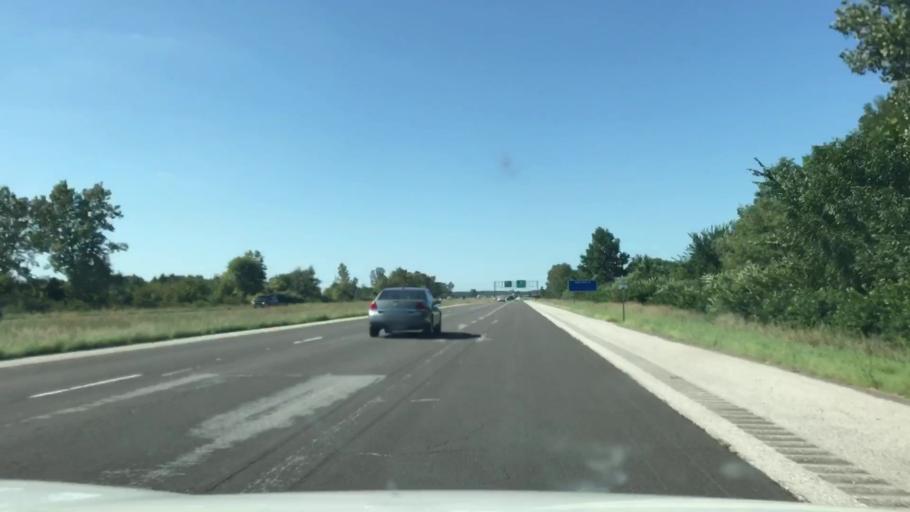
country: US
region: Illinois
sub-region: Madison County
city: South Roxana
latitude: 38.8432
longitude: -90.0456
